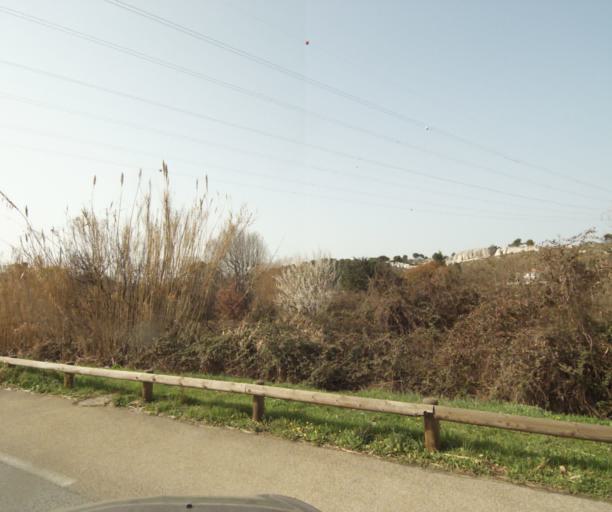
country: FR
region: Provence-Alpes-Cote d'Azur
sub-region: Departement des Bouches-du-Rhone
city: Les Pennes-Mirabeau
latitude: 43.4104
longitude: 5.3249
